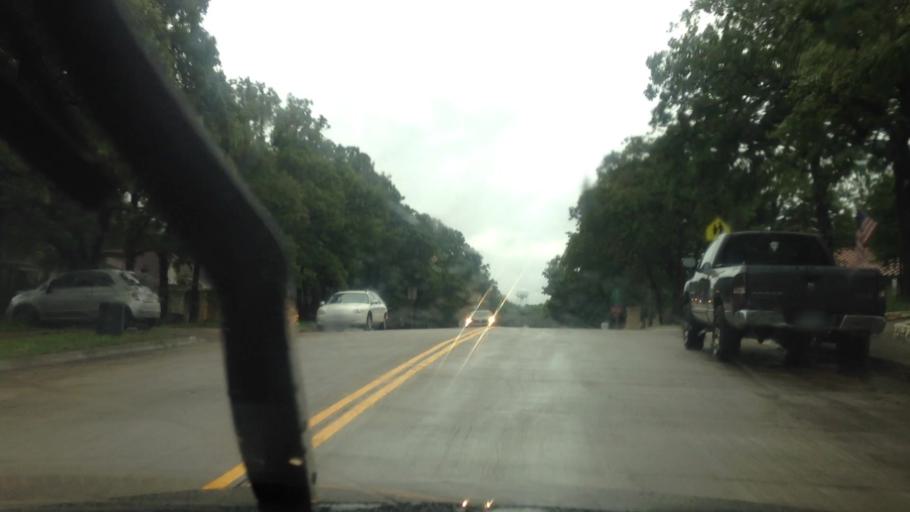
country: US
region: Texas
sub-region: Tarrant County
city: Watauga
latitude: 32.8817
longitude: -97.2350
